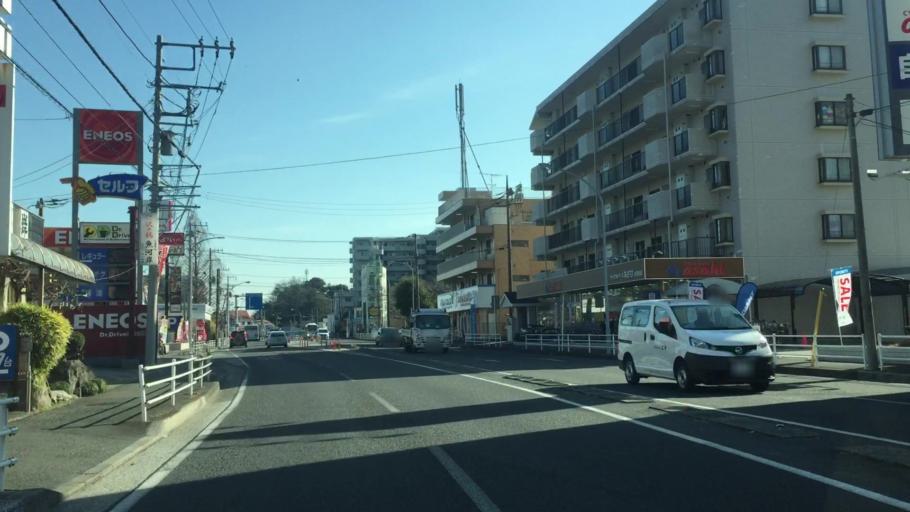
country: JP
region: Kanagawa
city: Zushi
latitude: 35.3466
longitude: 139.6089
